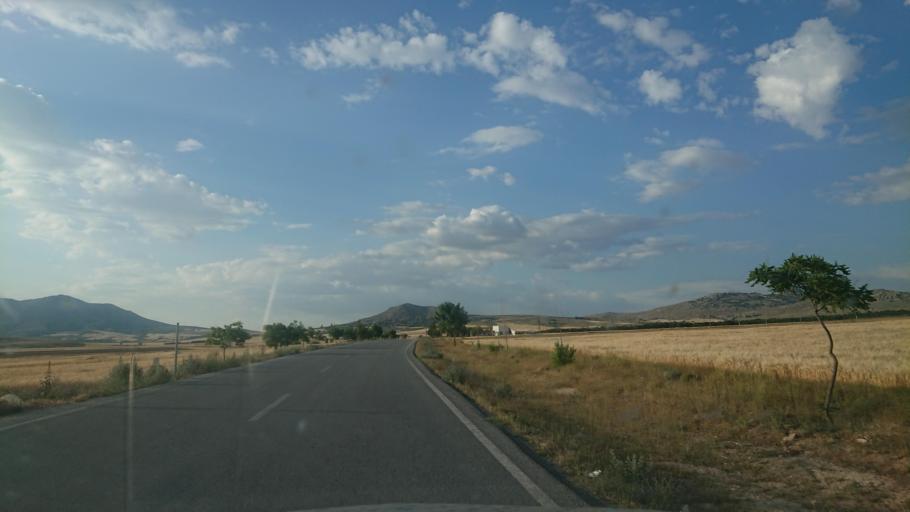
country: TR
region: Aksaray
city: Balci
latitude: 38.5645
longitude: 34.1050
